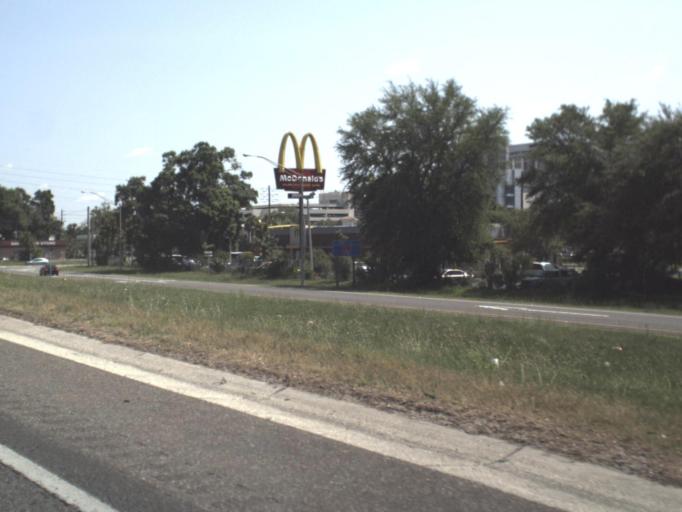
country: US
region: Florida
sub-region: Duval County
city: Jacksonville
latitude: 30.3458
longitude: -81.6681
